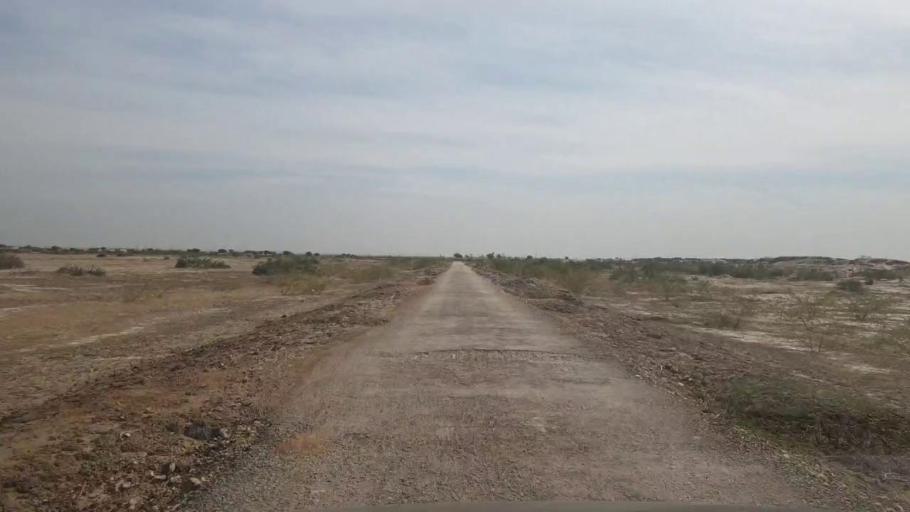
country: PK
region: Sindh
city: Kunri
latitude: 25.2165
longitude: 69.6223
